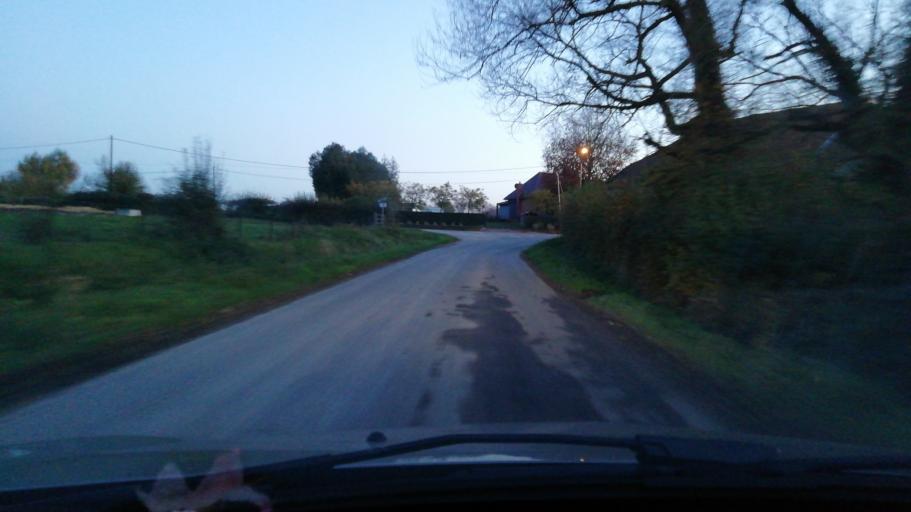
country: FR
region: Nord-Pas-de-Calais
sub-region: Departement du Nord
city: Marpent
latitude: 50.2660
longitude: 4.0875
